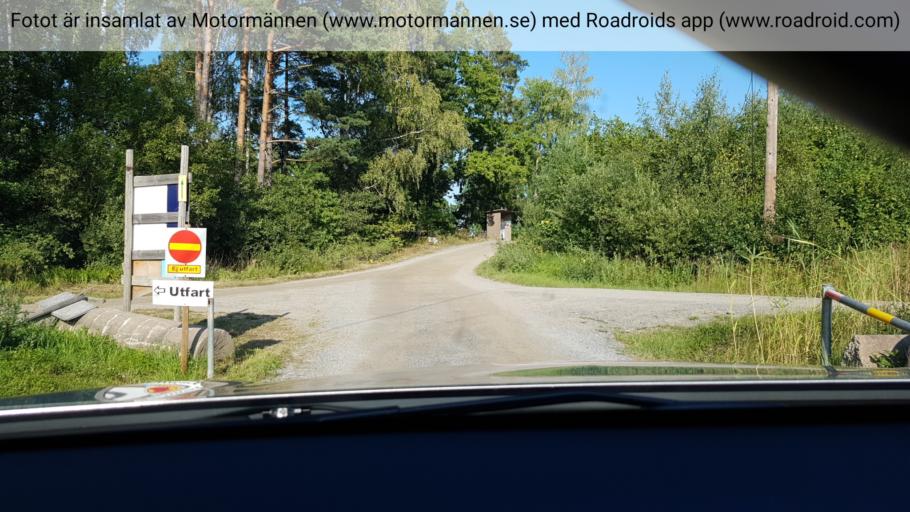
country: SE
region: Stockholm
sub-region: Nynashamns Kommun
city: Osmo
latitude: 58.9355
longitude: 17.9107
